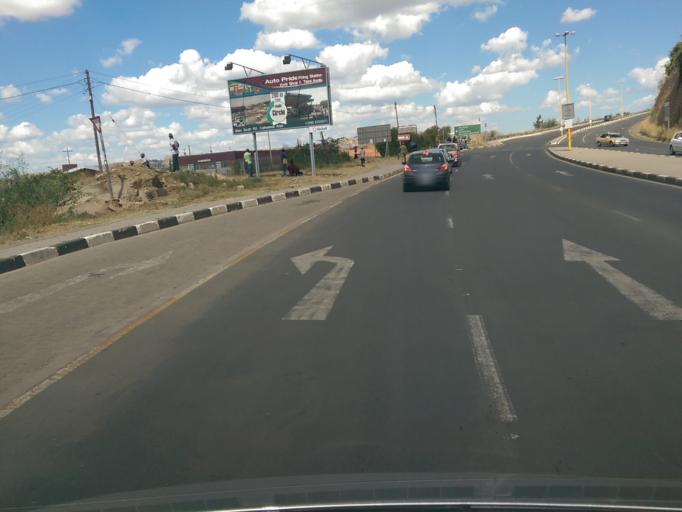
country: LS
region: Maseru
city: Maseru
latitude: -29.3168
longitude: 27.4914
